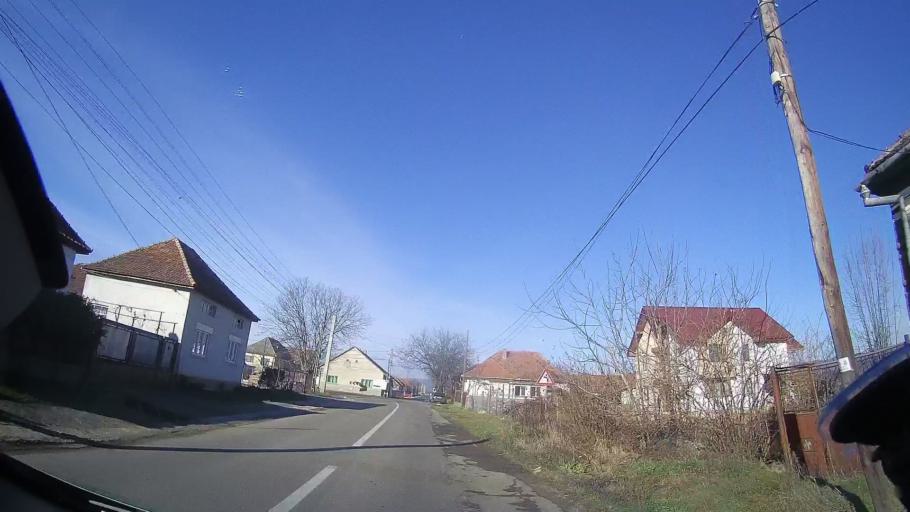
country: RO
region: Bihor
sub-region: Comuna Vadu Crisului
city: Vadu Crisului
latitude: 46.9908
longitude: 22.5097
